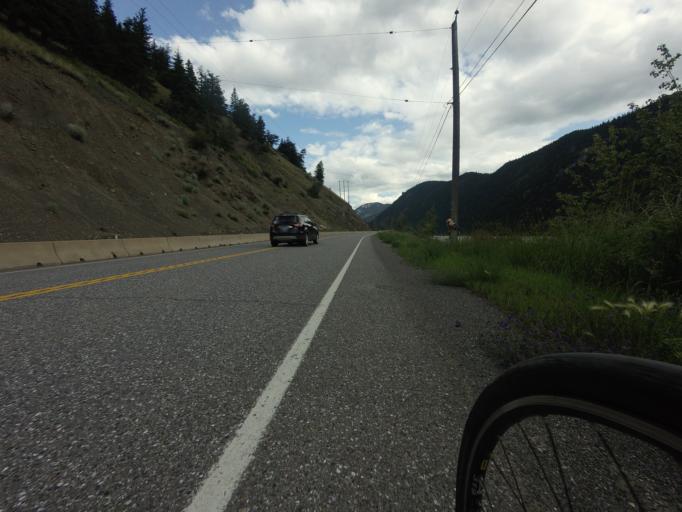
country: CA
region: British Columbia
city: Lillooet
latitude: 50.8685
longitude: -121.7368
